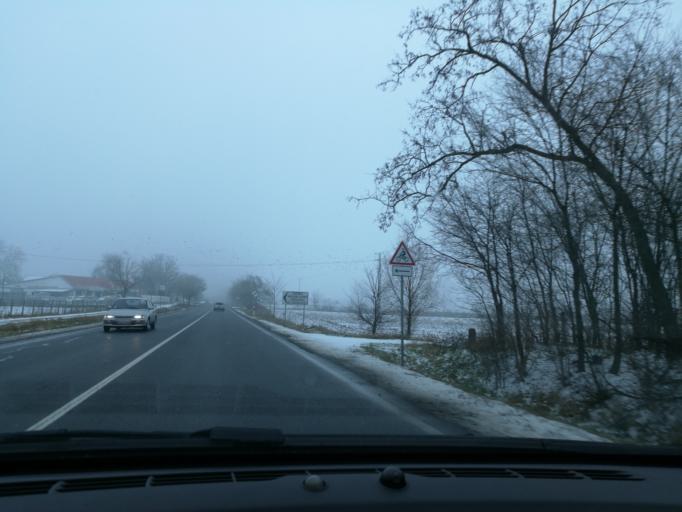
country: HU
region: Szabolcs-Szatmar-Bereg
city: Nyirpazony
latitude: 47.9950
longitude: 21.8073
